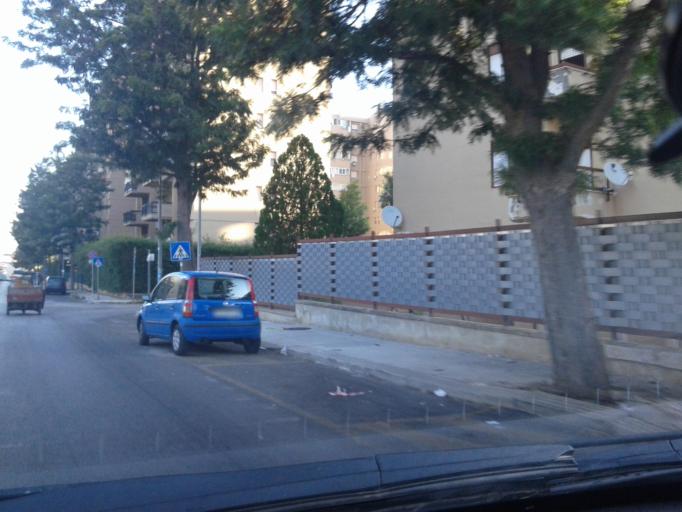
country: IT
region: Sicily
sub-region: Palermo
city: Ciaculli
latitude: 38.0846
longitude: 13.3621
